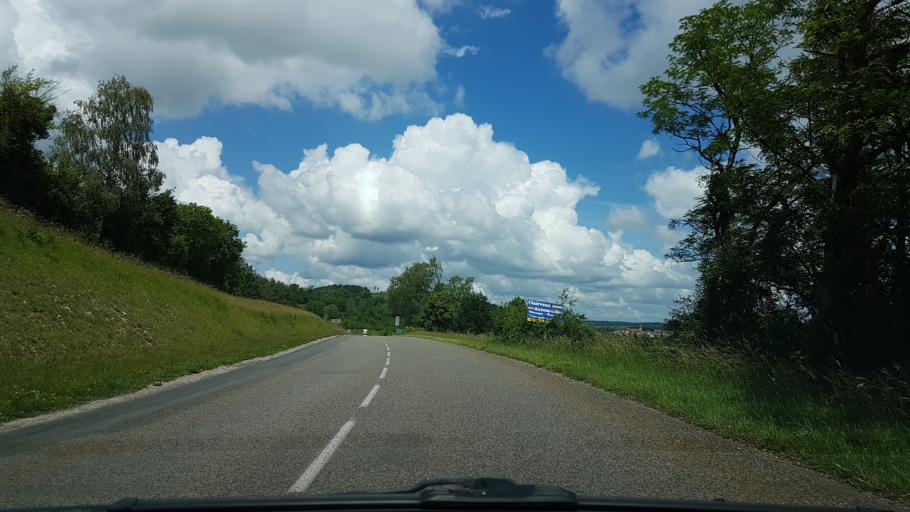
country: FR
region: Franche-Comte
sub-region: Departement du Jura
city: Clairvaux-les-Lacs
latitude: 46.5586
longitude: 5.7450
